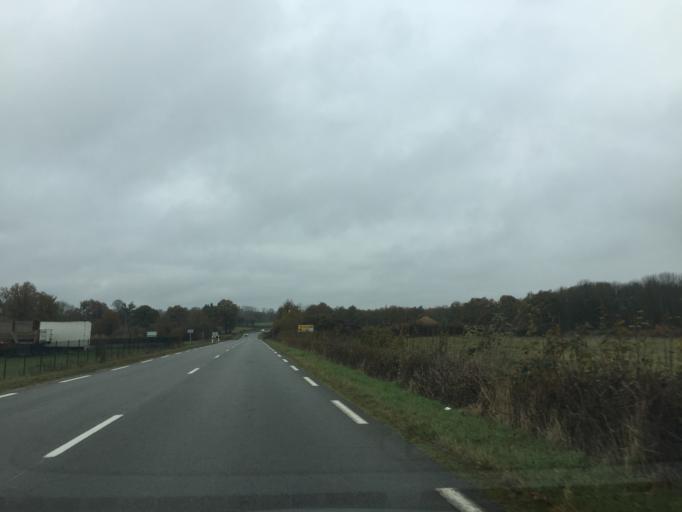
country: FR
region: Limousin
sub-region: Departement de la Creuse
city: Gouzon
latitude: 46.1267
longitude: 2.1879
